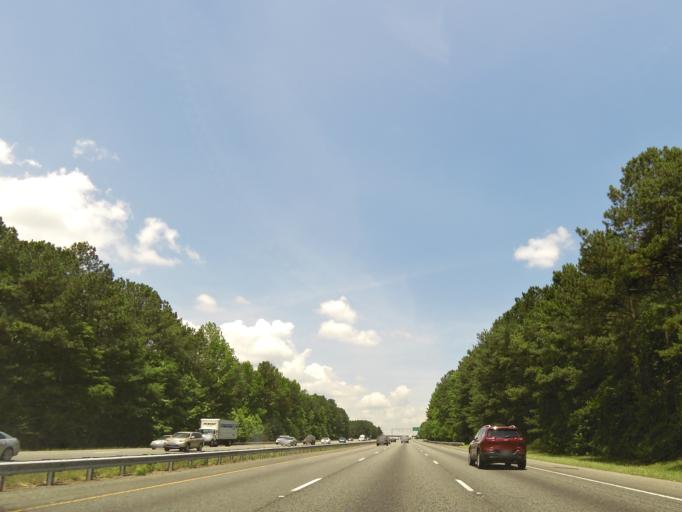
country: US
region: Georgia
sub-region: Butts County
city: Indian Springs
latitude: 33.1593
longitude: -84.0366
